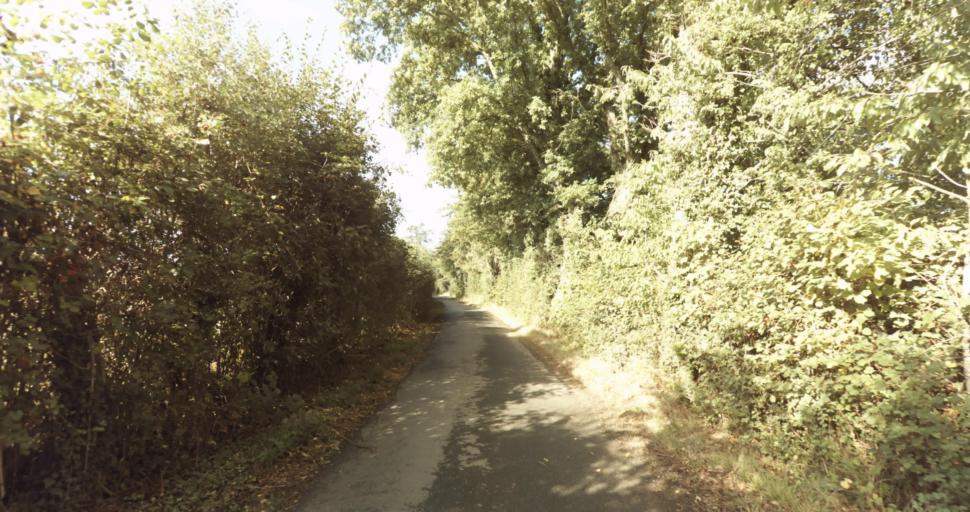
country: FR
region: Lower Normandy
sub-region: Departement de l'Orne
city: Vimoutiers
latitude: 48.9159
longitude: 0.1178
